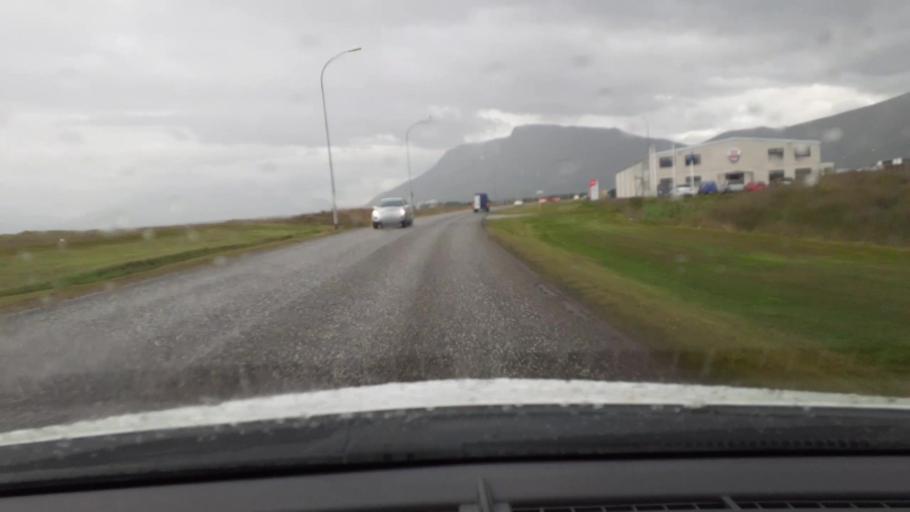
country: IS
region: West
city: Akranes
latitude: 64.3267
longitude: -22.0632
